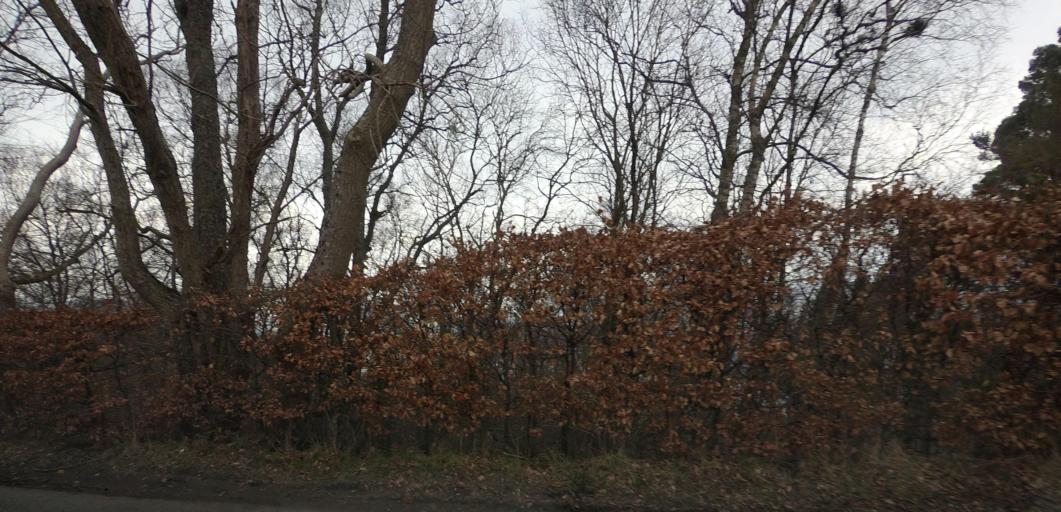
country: GB
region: Scotland
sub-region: Perth and Kinross
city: Comrie
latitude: 56.5052
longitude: -4.1405
